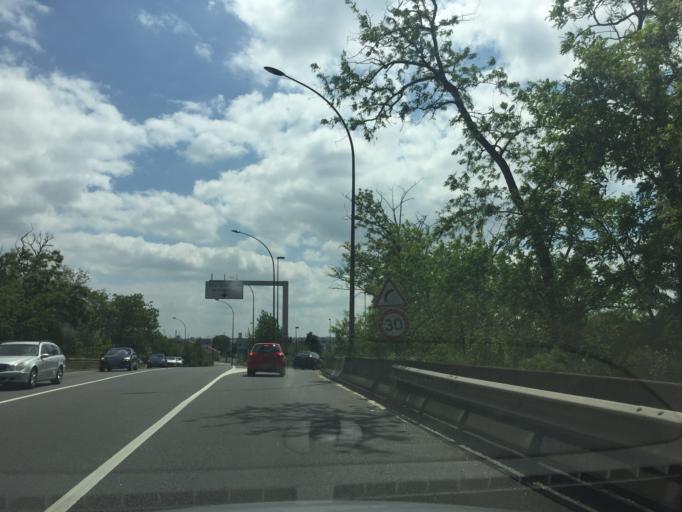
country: FR
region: Midi-Pyrenees
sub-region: Departement de la Haute-Garonne
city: Aucamville
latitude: 43.6496
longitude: 1.4253
